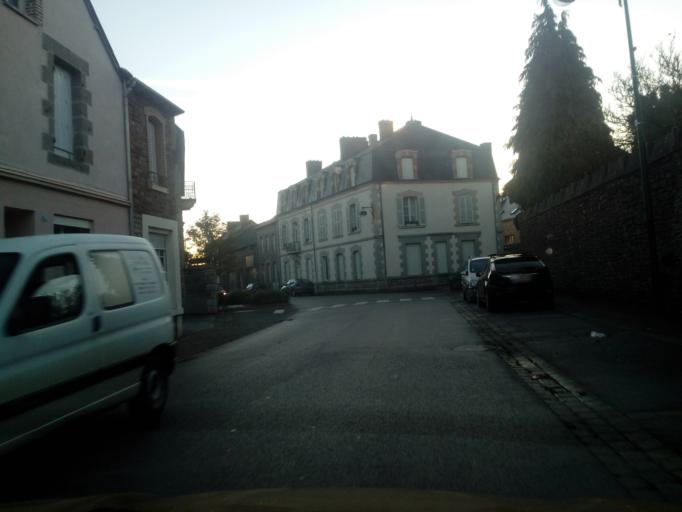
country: FR
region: Brittany
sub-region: Departement du Morbihan
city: Mauron
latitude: 48.0833
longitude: -2.2875
